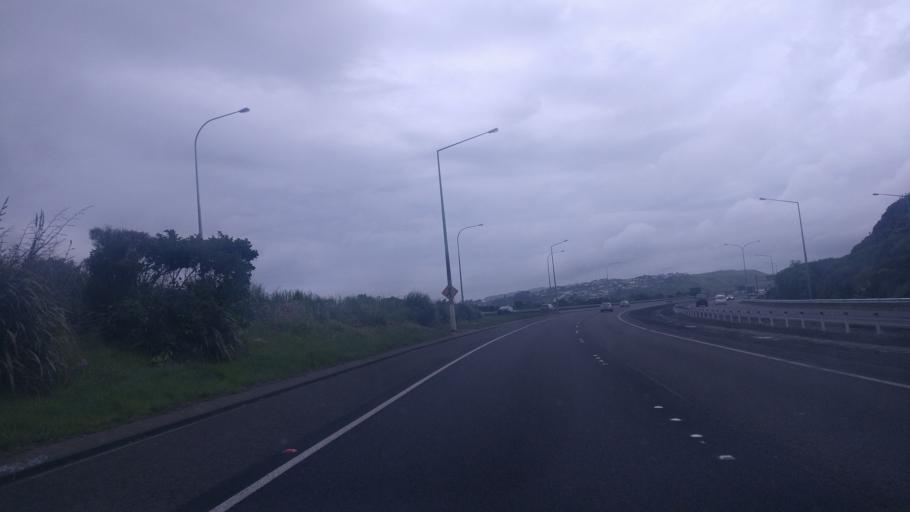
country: NZ
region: Wellington
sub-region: Porirua City
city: Porirua
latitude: -41.1308
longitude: 174.8441
